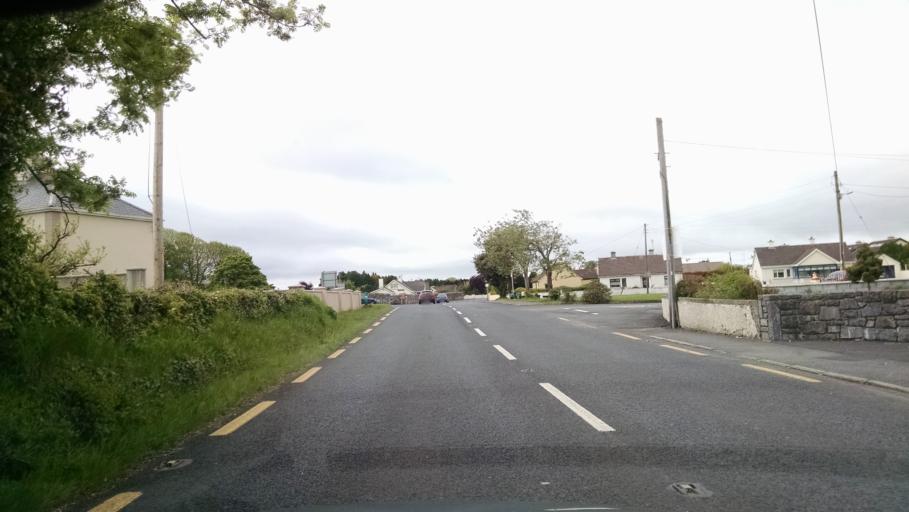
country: IE
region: Connaught
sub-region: County Galway
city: Moycullen
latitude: 53.4748
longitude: -9.0936
